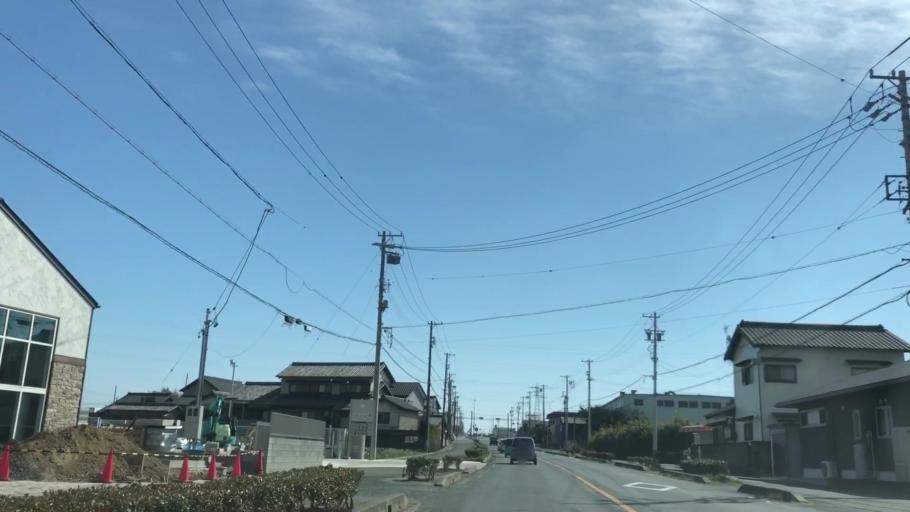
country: JP
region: Aichi
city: Toyohashi
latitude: 34.7126
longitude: 137.4076
